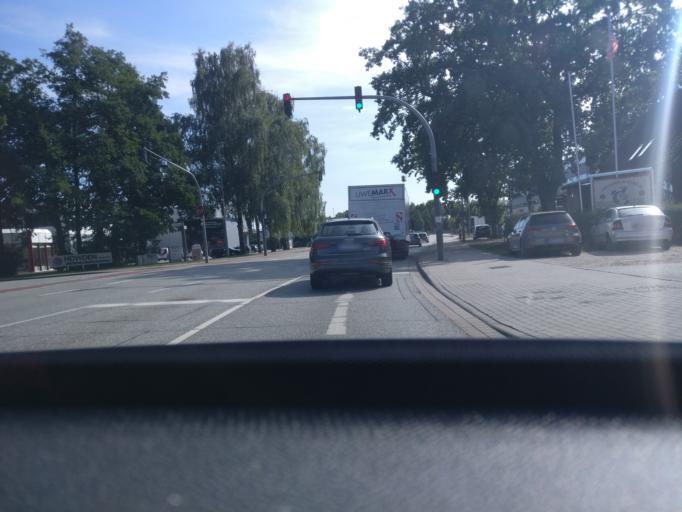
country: DE
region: Hamburg
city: Langenhorn
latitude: 53.6599
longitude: 9.9809
